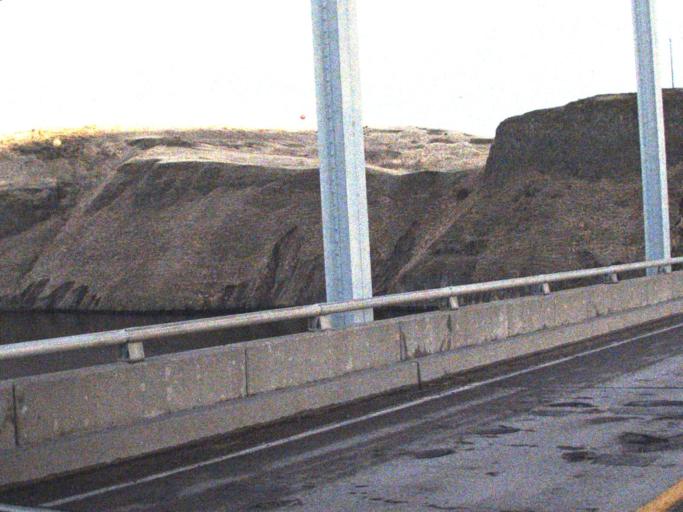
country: US
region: Washington
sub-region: Garfield County
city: Pomeroy
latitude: 46.6268
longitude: -117.7990
